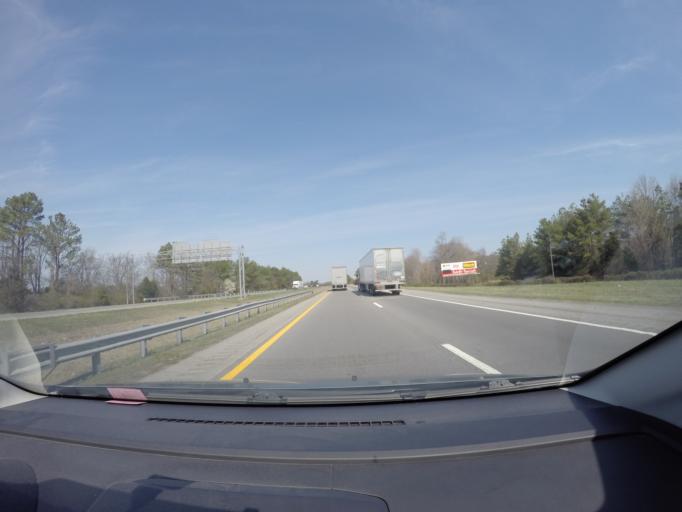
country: US
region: Tennessee
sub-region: Rutherford County
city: Murfreesboro
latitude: 35.7938
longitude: -86.3777
